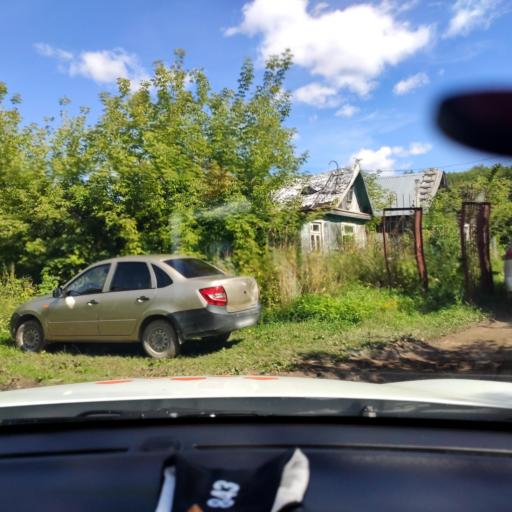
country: RU
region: Tatarstan
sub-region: Gorod Kazan'
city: Kazan
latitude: 55.8255
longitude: 49.2054
